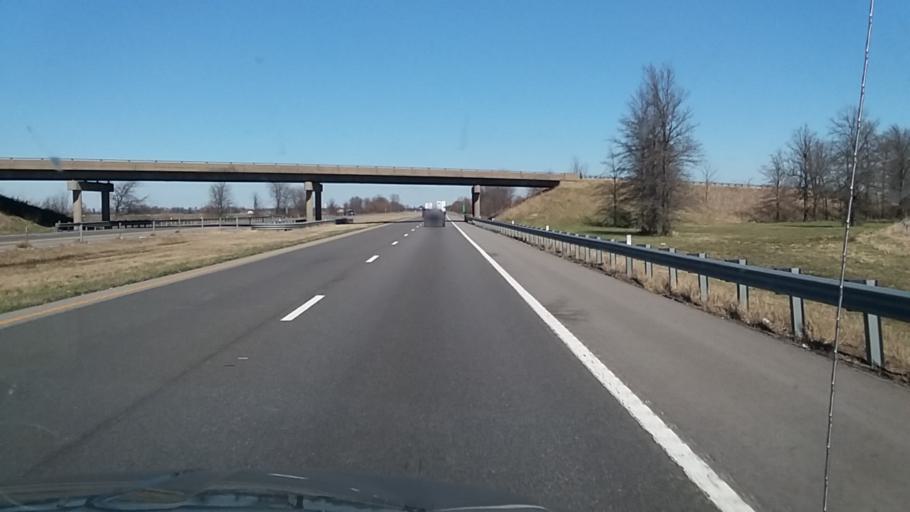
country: US
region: Missouri
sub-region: New Madrid County
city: Portageville
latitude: 36.4827
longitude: -89.6324
